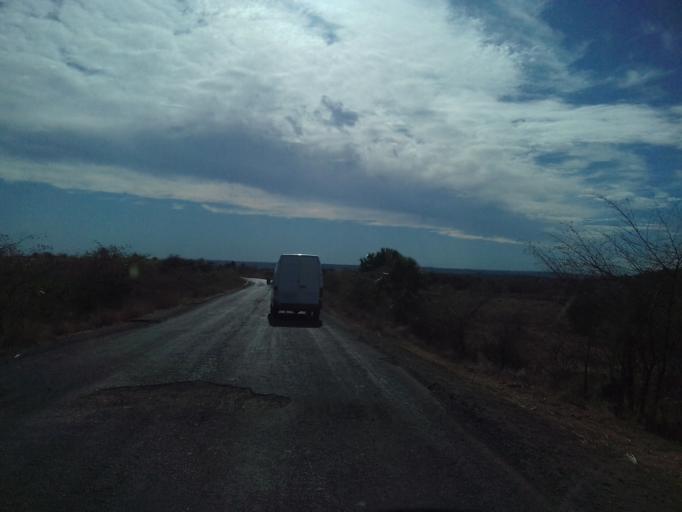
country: MG
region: Sofia
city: Antsohihy
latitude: -15.3484
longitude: 47.7755
